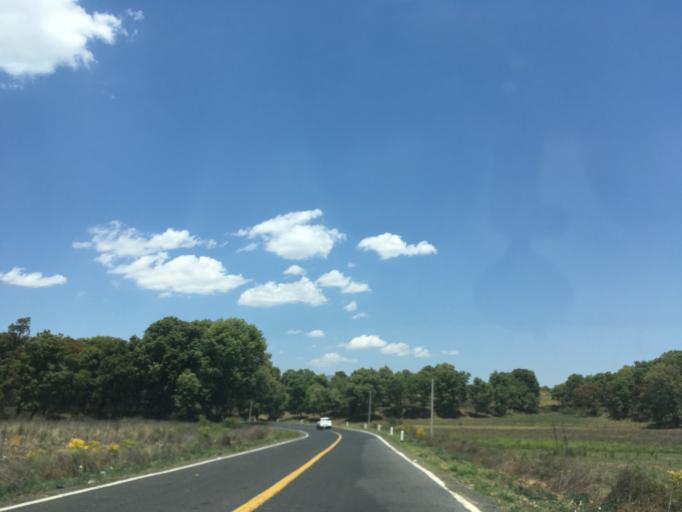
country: MX
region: Michoacan
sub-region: Chilchota
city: Tacuro (Santa Maria Tacuro)
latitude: 19.8070
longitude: -102.0250
